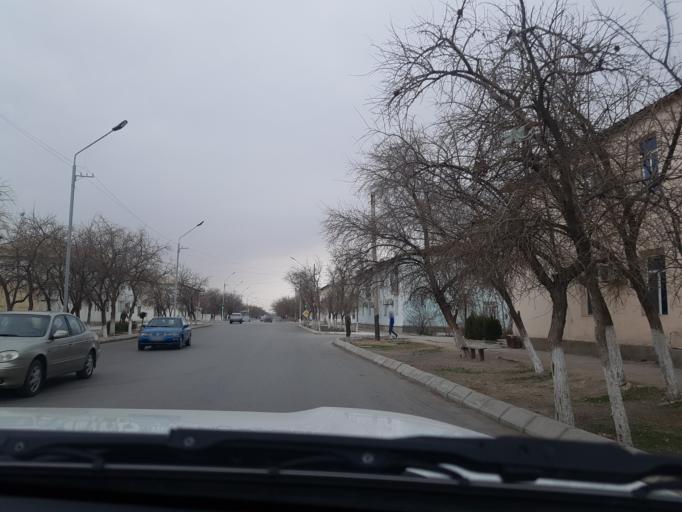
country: TM
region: Balkan
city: Balkanabat
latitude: 39.5066
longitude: 54.3579
